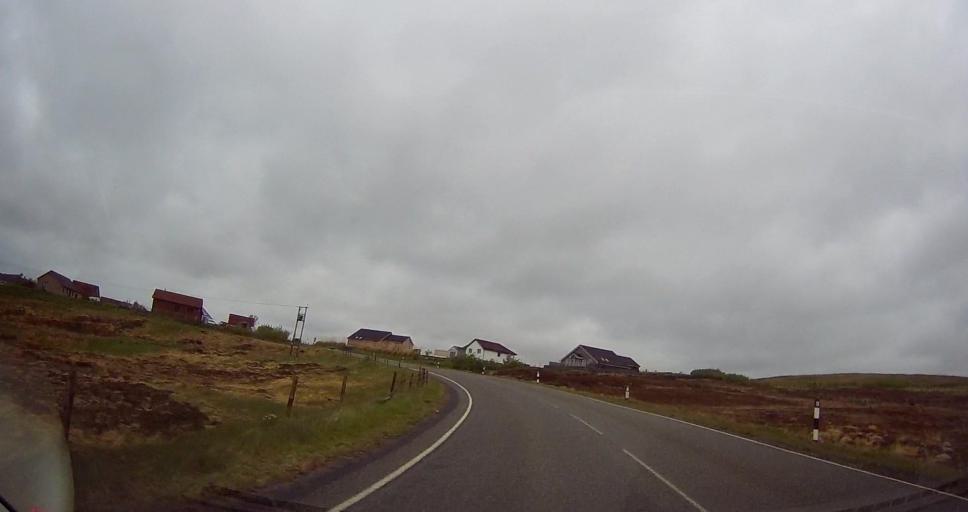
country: GB
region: Scotland
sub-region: Shetland Islands
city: Lerwick
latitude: 60.3852
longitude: -1.3425
